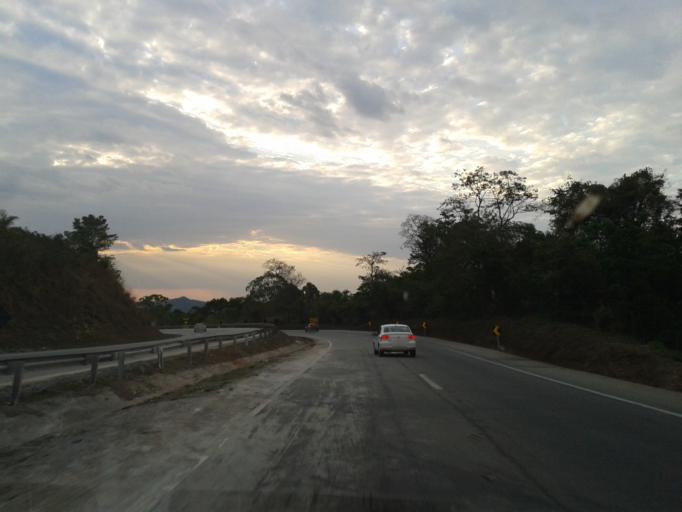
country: BR
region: Minas Gerais
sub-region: Mateus Leme
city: Mateus Leme
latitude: -19.9373
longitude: -44.4467
